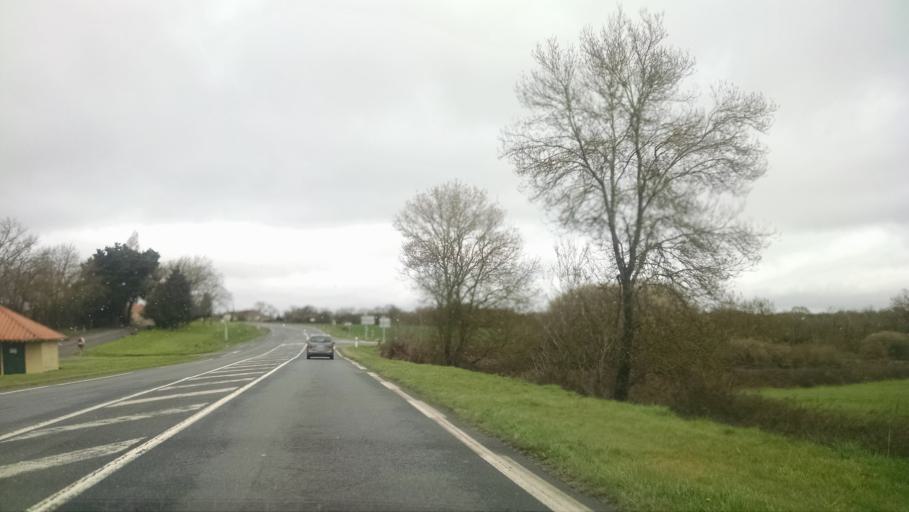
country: FR
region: Pays de la Loire
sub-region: Departement de la Loire-Atlantique
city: Aigrefeuille-sur-Maine
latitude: 47.0688
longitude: -1.3914
